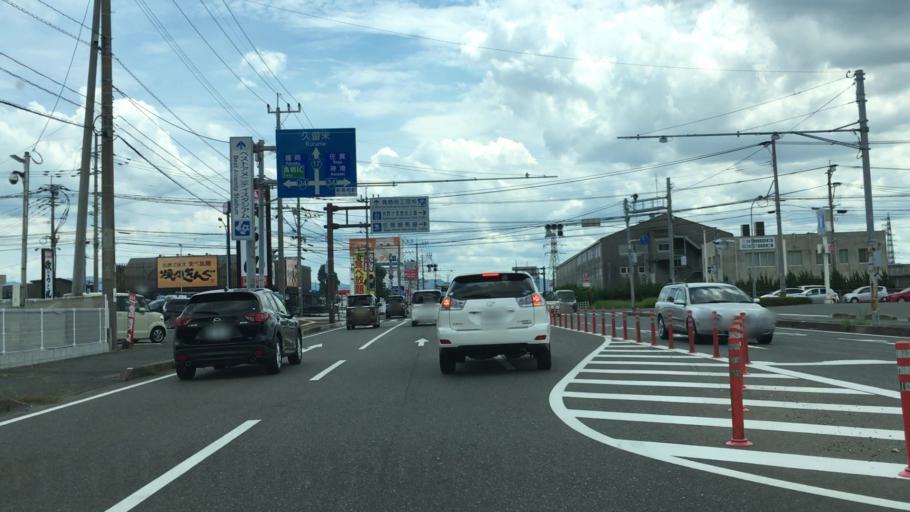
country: JP
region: Saga Prefecture
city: Tosu
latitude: 33.3655
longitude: 130.5016
